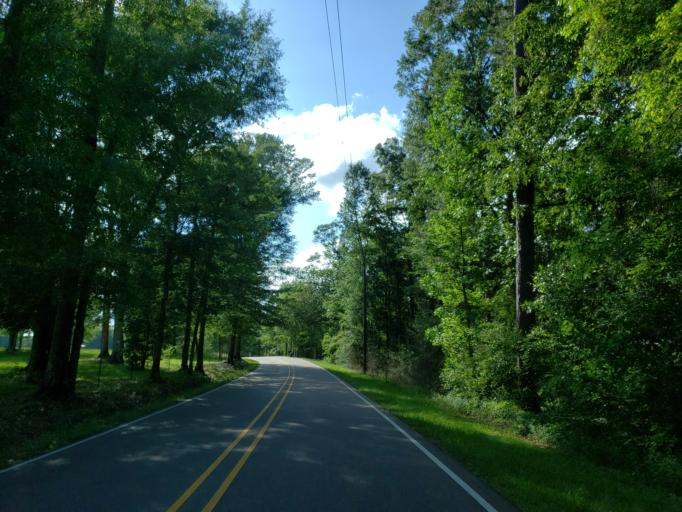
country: US
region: Mississippi
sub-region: Lamar County
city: Sumrall
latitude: 31.3544
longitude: -89.4768
